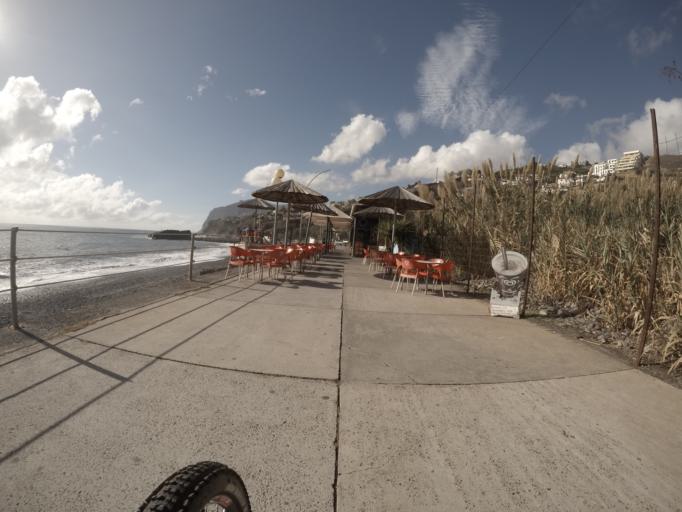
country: PT
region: Madeira
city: Camara de Lobos
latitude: 32.6410
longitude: -16.9531
